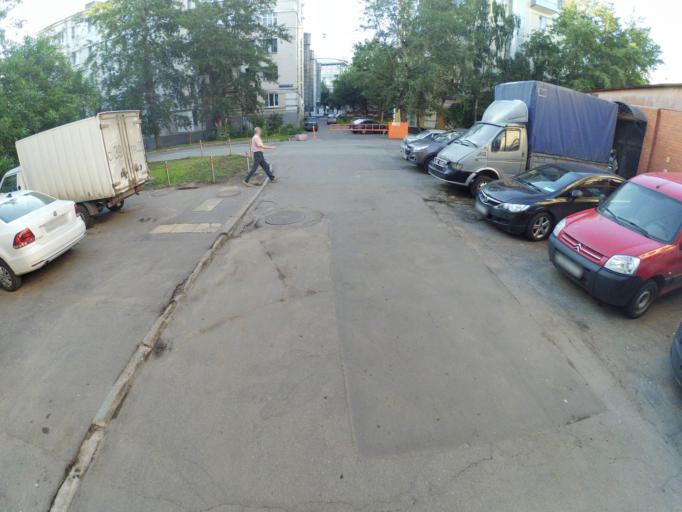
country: RU
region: Moskovskaya
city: Presnenskiy
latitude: 55.7594
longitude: 37.5522
